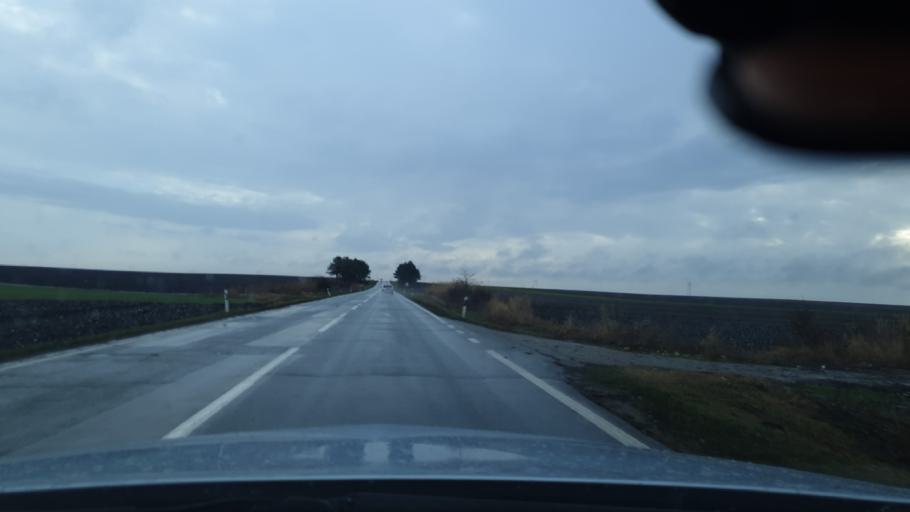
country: RS
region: Autonomna Pokrajina Vojvodina
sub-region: Juznobanatski Okrug
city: Kovin
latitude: 44.8322
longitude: 20.8270
